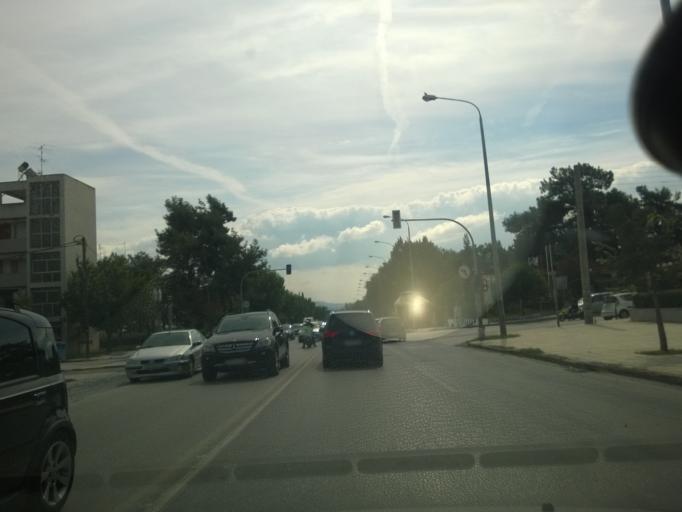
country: GR
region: Central Macedonia
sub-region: Nomos Thessalonikis
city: Kalamaria
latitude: 40.5704
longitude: 22.9730
